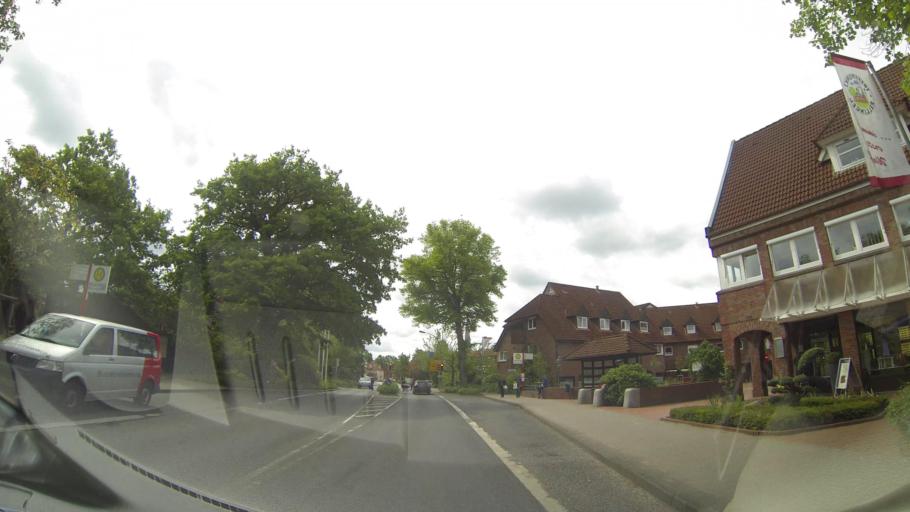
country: DE
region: Schleswig-Holstein
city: Rellingen
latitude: 53.6516
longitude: 9.8295
